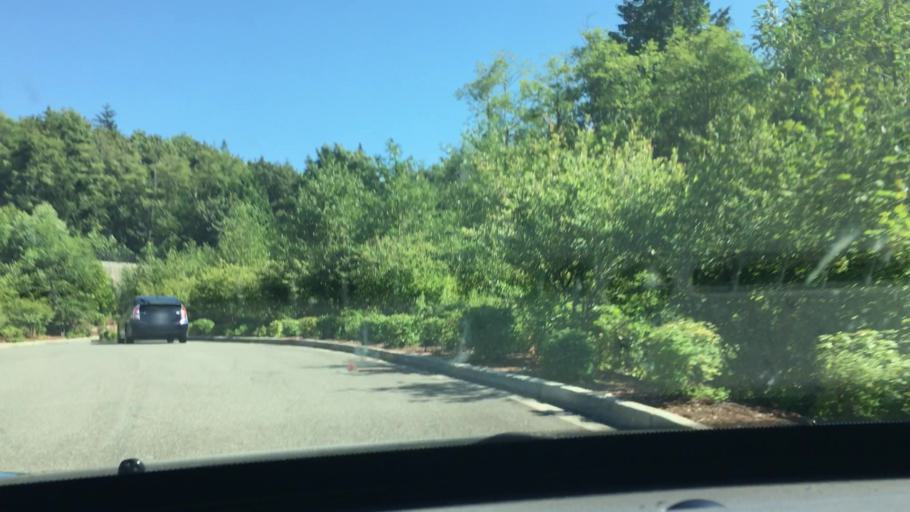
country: US
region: Washington
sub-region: King County
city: Newcastle
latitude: 47.5372
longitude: -122.1163
